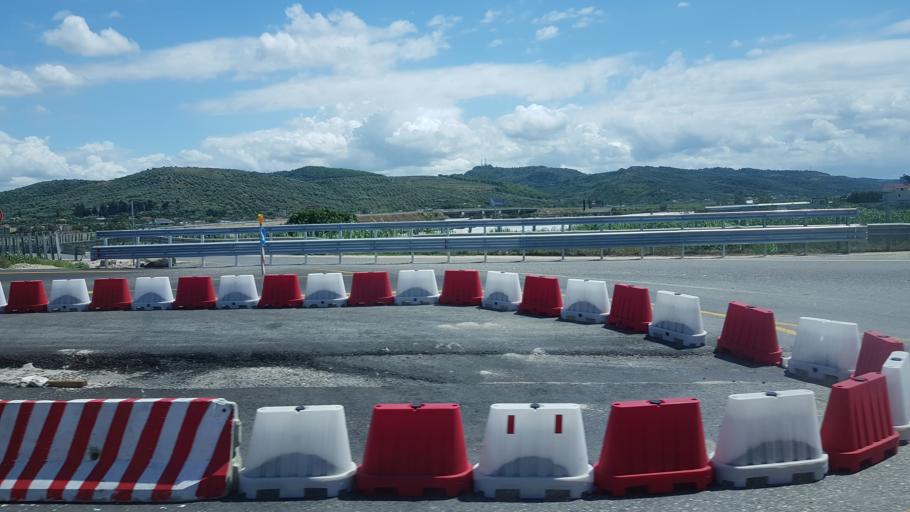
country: AL
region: Fier
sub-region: Rrethi i Fierit
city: Levan
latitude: 40.6702
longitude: 19.4786
